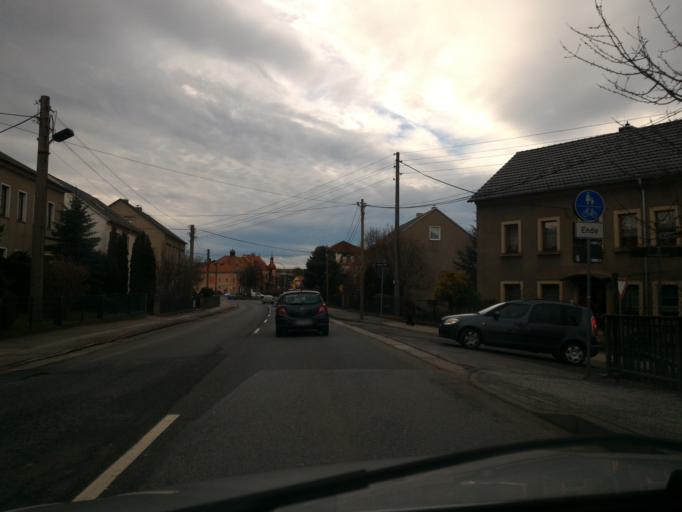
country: DE
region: Saxony
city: Radeberg
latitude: 51.0631
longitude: 13.8869
